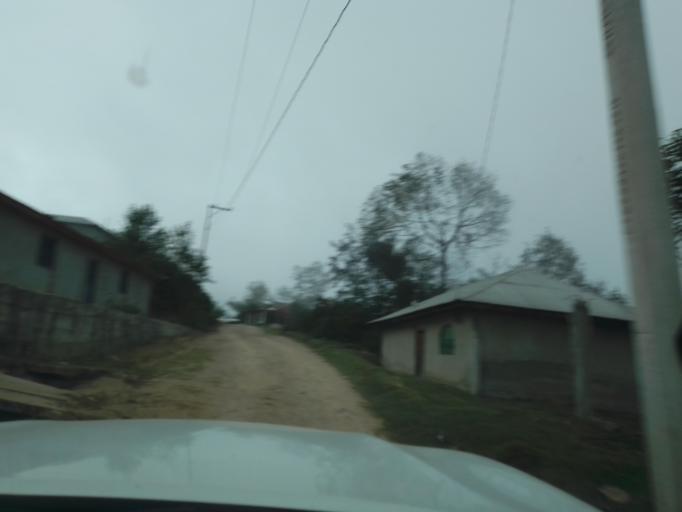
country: MX
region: Chiapas
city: Motozintla de Mendoza
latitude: 15.2218
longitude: -92.2219
